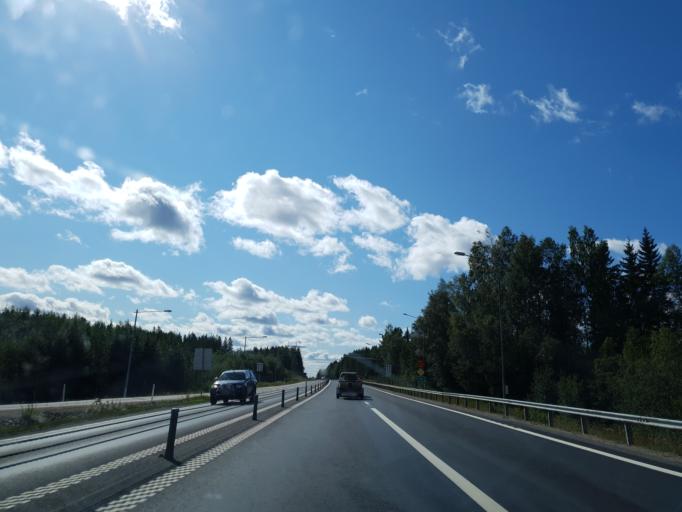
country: SE
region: Vaesterbotten
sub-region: Nordmalings Kommun
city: Nordmaling
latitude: 63.5479
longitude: 19.4127
